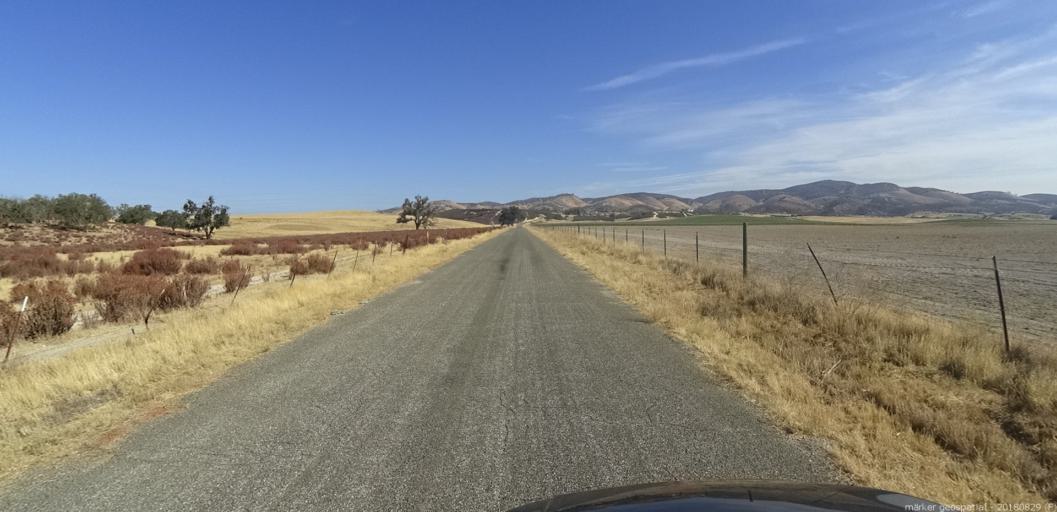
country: US
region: California
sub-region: Monterey County
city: King City
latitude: 35.9669
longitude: -121.1175
